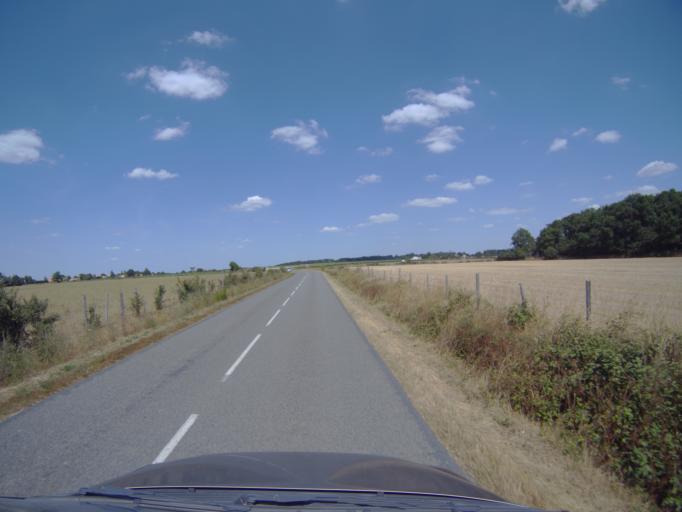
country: FR
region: Pays de la Loire
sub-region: Departement de la Loire-Atlantique
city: La Planche
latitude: 47.0323
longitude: -1.4184
